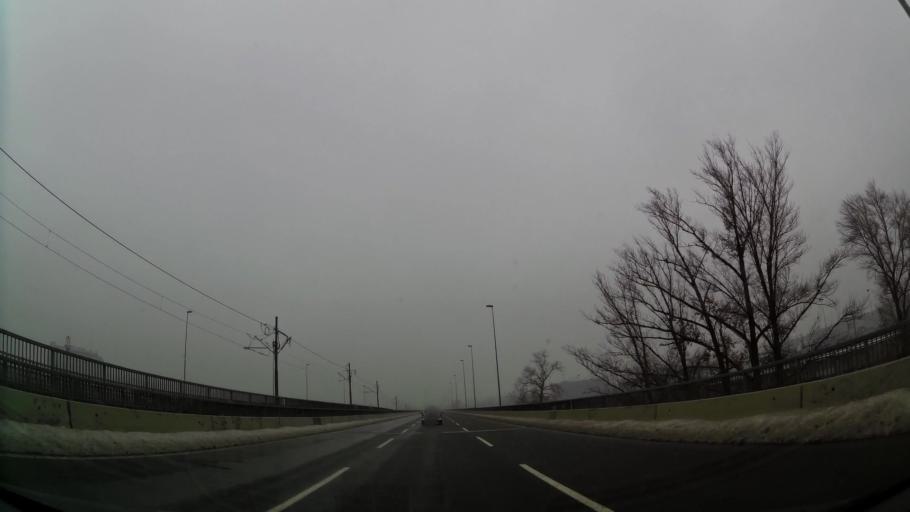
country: RS
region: Central Serbia
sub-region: Belgrade
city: Novi Beograd
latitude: 44.8058
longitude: 20.4183
